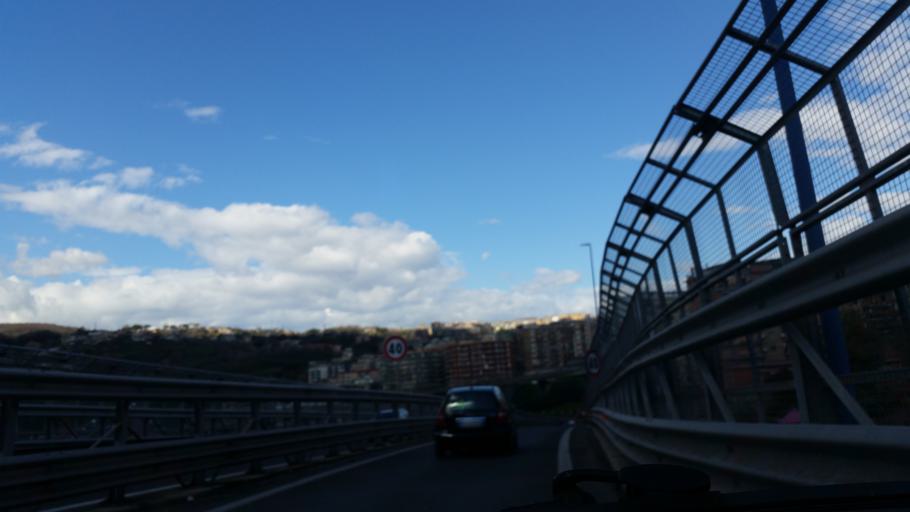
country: IT
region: Campania
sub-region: Provincia di Napoli
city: Napoli
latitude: 40.8428
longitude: 14.2187
